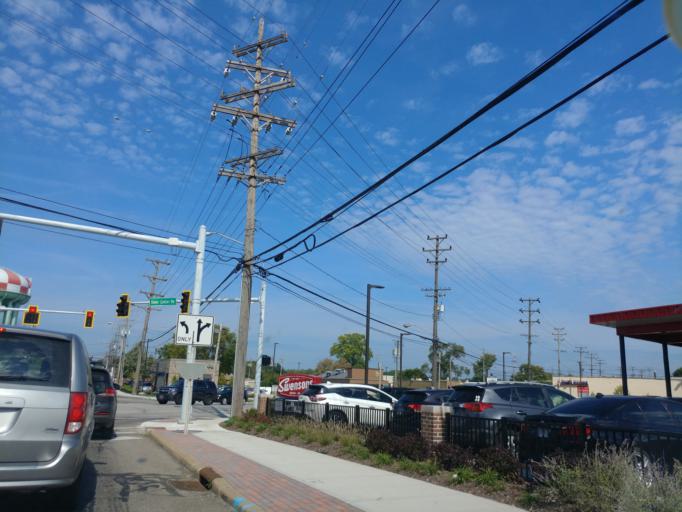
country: US
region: Ohio
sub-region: Cuyahoga County
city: North Olmsted
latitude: 41.4155
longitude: -81.9233
